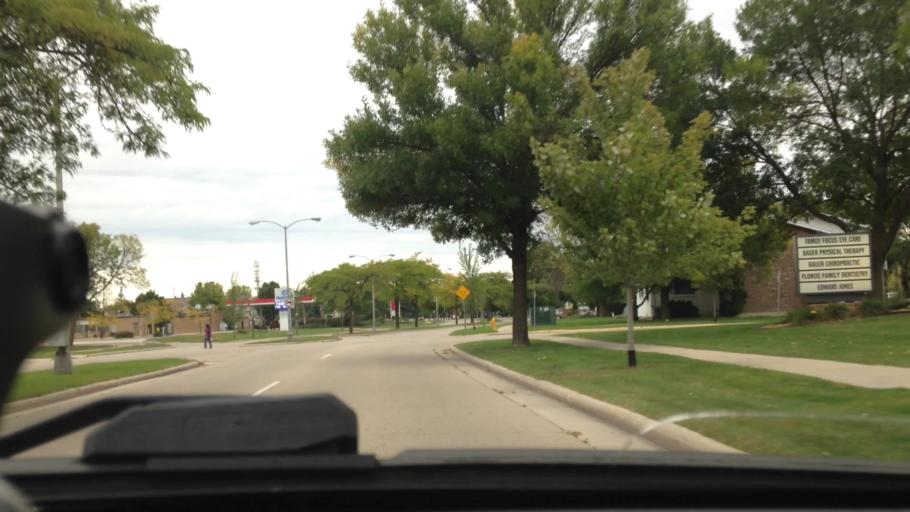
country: US
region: Wisconsin
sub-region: Fond du Lac County
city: North Fond du Lac
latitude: 43.7873
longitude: -88.4729
